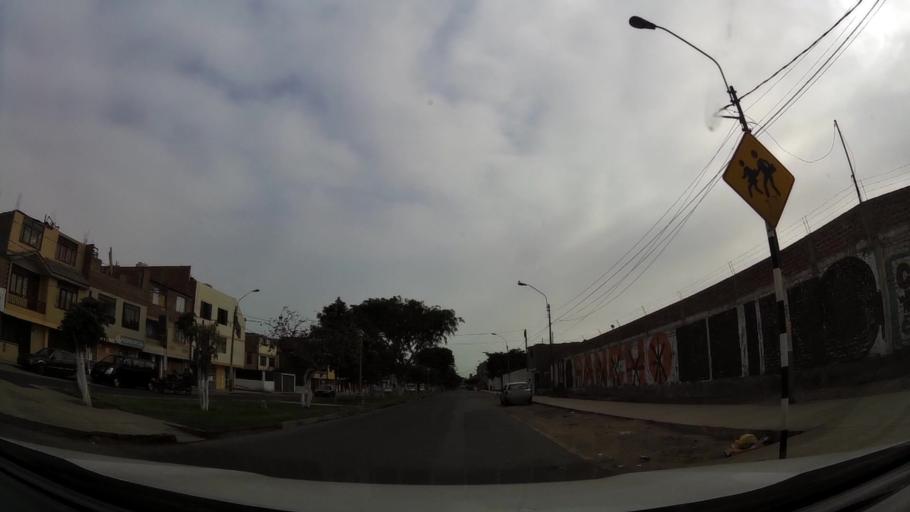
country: PE
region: Callao
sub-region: Callao
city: Callao
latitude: -12.0149
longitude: -77.0899
